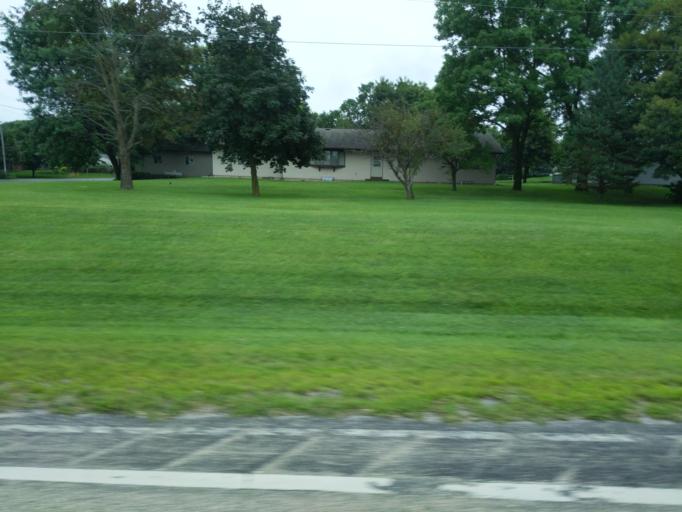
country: US
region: Wisconsin
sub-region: Sauk County
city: Sauk City
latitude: 43.2529
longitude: -89.7198
